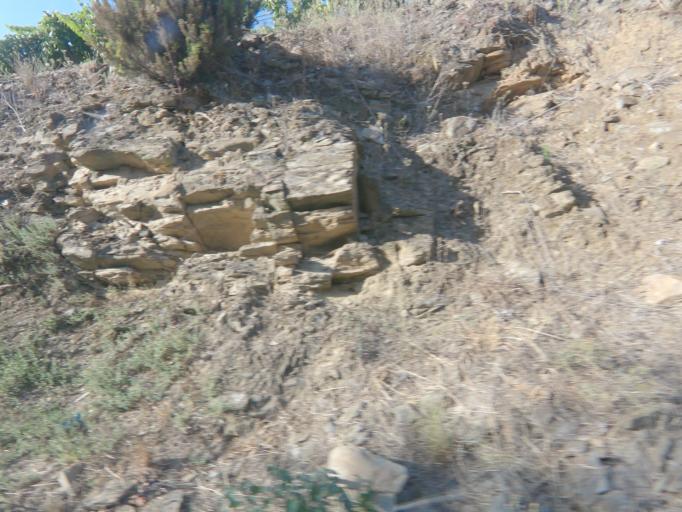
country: PT
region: Vila Real
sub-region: Sabrosa
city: Vilela
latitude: 41.1826
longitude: -7.5839
